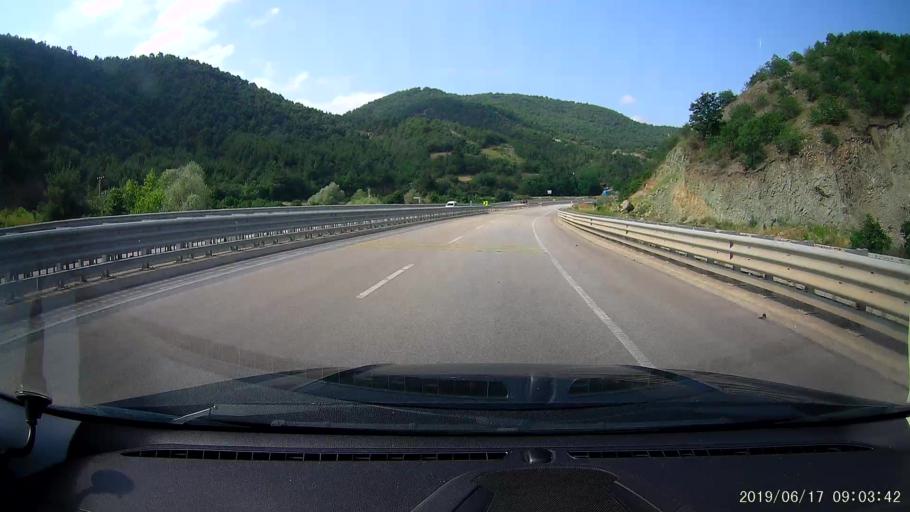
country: TR
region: Amasya
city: Tasova
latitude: 40.7516
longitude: 36.3019
